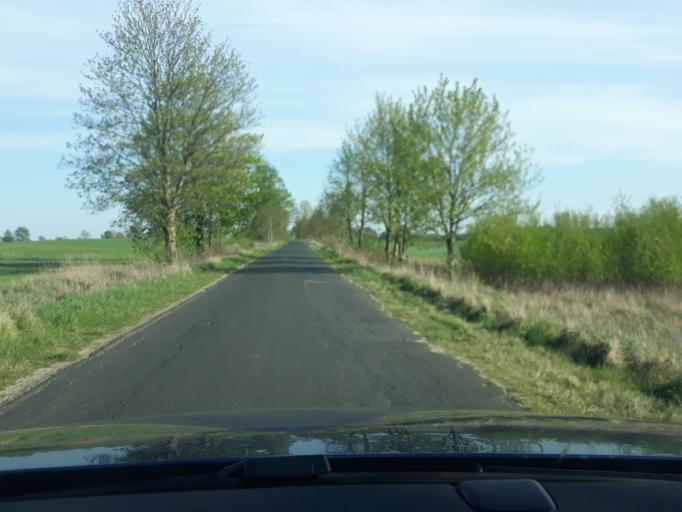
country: PL
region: Pomeranian Voivodeship
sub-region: Powiat czluchowski
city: Przechlewo
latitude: 53.8539
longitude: 17.3515
